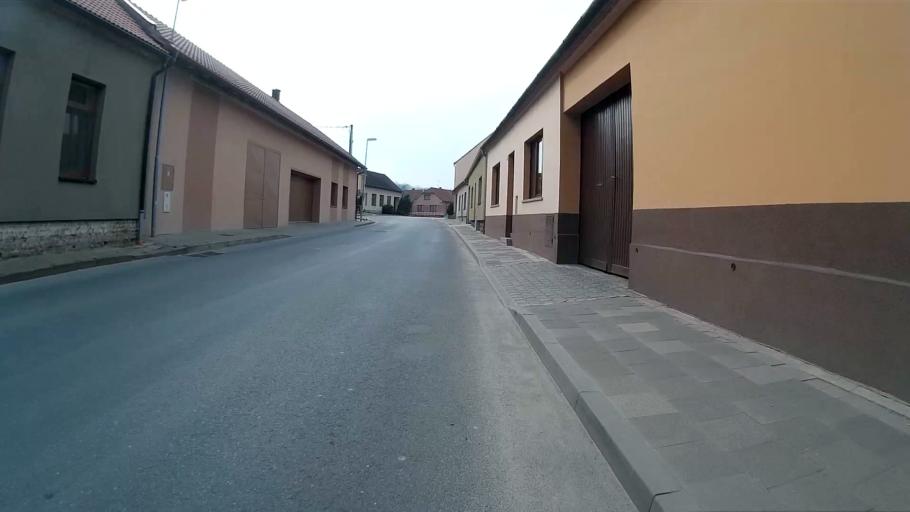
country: CZ
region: South Moravian
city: Dolni Kounice
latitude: 49.0703
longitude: 16.4447
